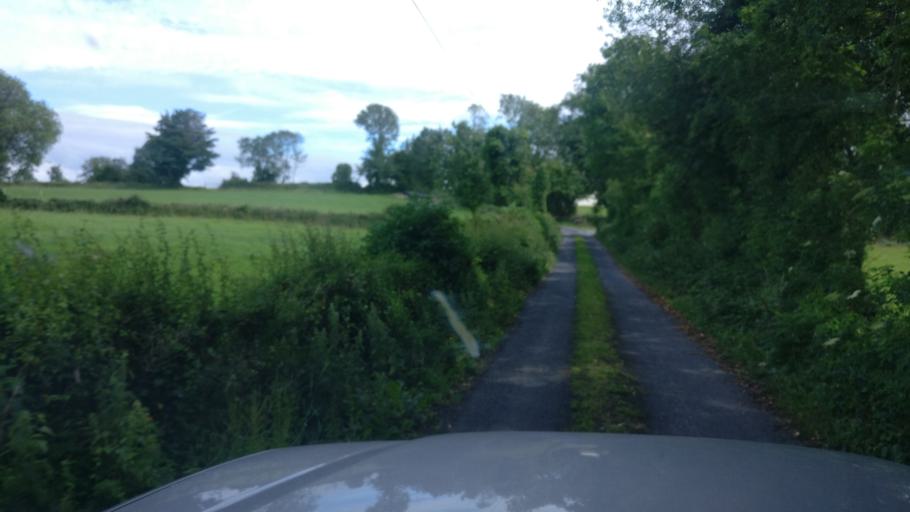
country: IE
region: Connaught
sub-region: County Galway
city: Gort
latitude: 53.0729
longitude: -8.7700
